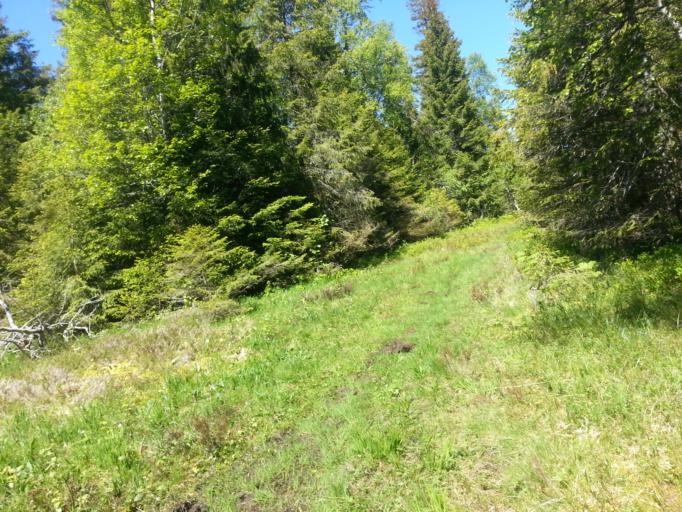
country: NO
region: Sor-Trondelag
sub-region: Trondheim
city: Trondheim
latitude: 63.4066
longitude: 10.2887
